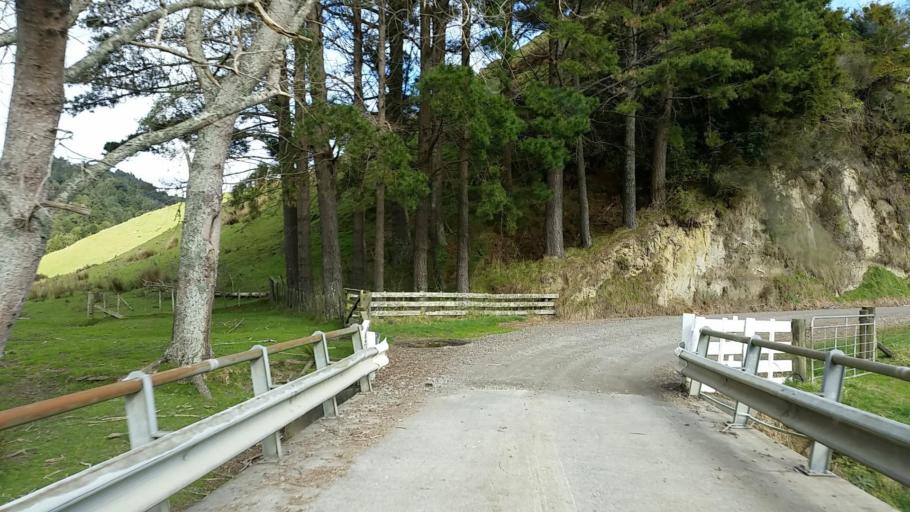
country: NZ
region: Taranaki
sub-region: New Plymouth District
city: Waitara
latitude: -39.1424
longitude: 174.5685
